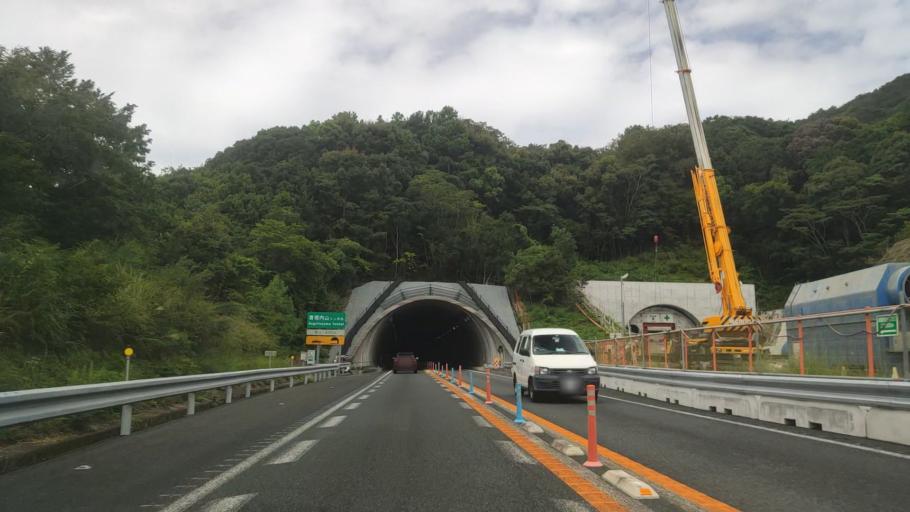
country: JP
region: Wakayama
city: Gobo
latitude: 33.8487
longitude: 135.2167
